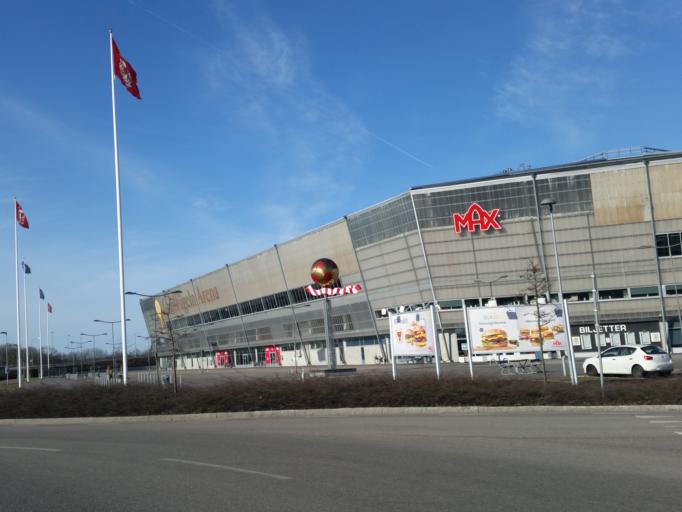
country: SE
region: Kalmar
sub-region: Kalmar Kommun
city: Lindsdal
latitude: 56.6901
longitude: 16.3139
